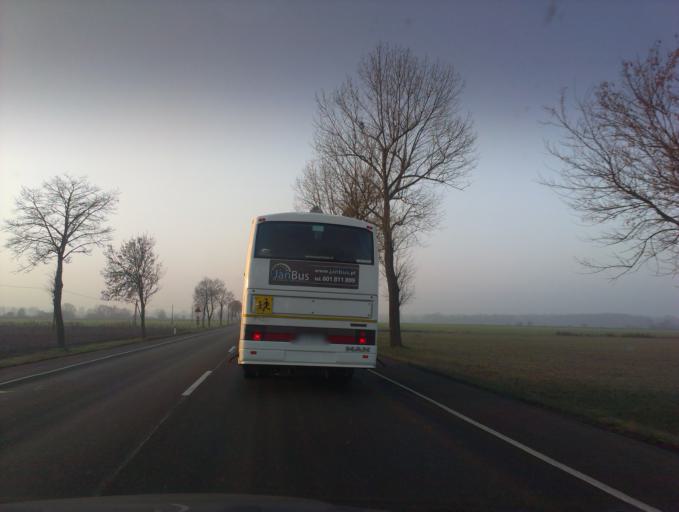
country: PL
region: Greater Poland Voivodeship
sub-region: Powiat obornicki
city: Rogozno
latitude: 52.7468
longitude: 16.9538
